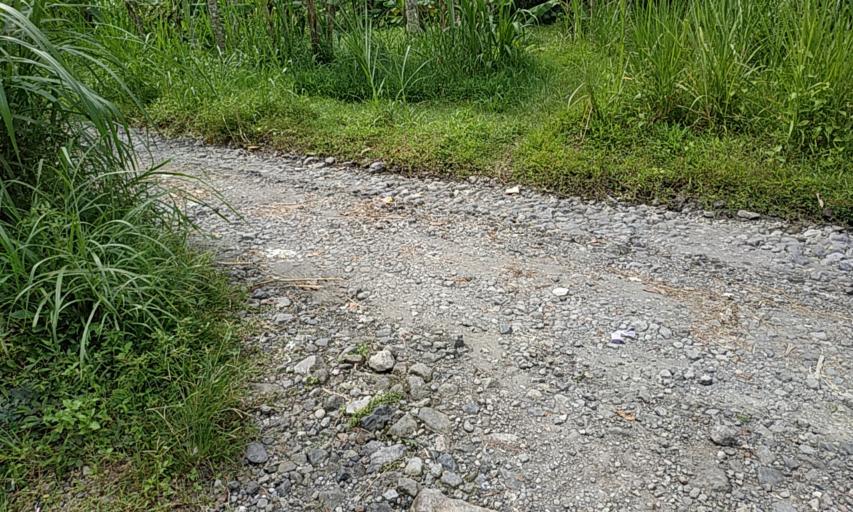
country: ID
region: Central Java
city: Jogonalan
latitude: -7.6340
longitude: 110.4871
